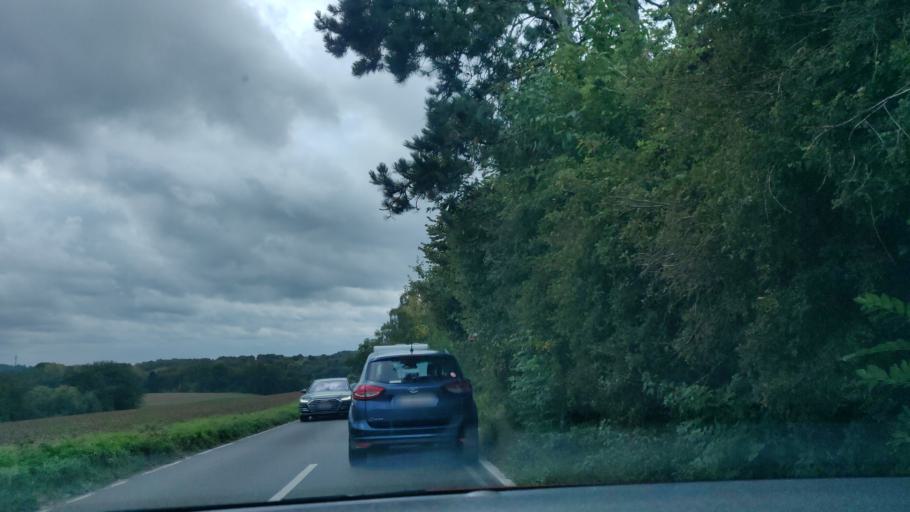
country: DE
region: North Rhine-Westphalia
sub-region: Regierungsbezirk Dusseldorf
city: Heiligenhaus
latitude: 51.2938
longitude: 6.9345
